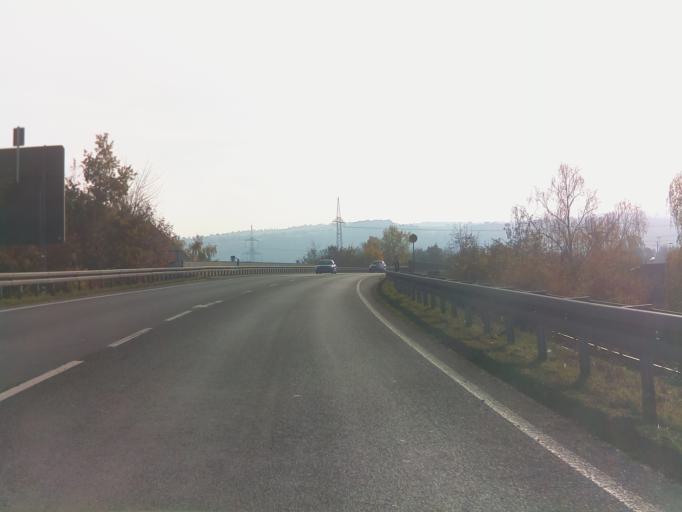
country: DE
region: Bavaria
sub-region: Regierungsbezirk Unterfranken
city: Ebelsbach
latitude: 49.9833
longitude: 10.6711
